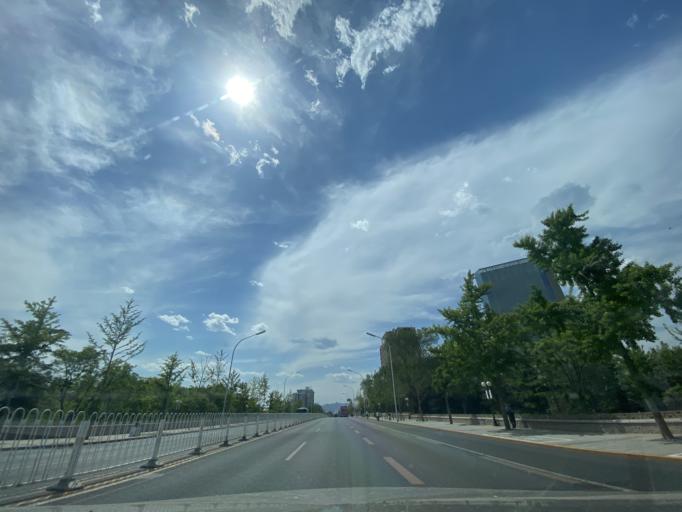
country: CN
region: Beijing
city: Lugu
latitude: 39.9062
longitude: 116.2009
